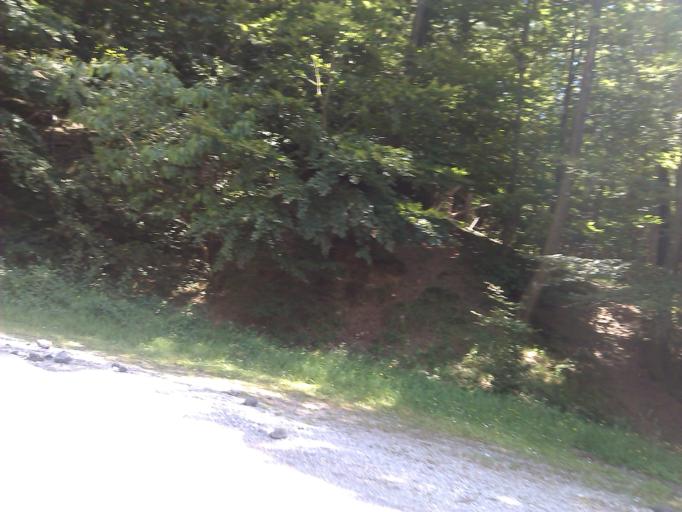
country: IT
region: Tuscany
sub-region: Provincia di Prato
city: Cantagallo
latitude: 43.9966
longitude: 11.0240
